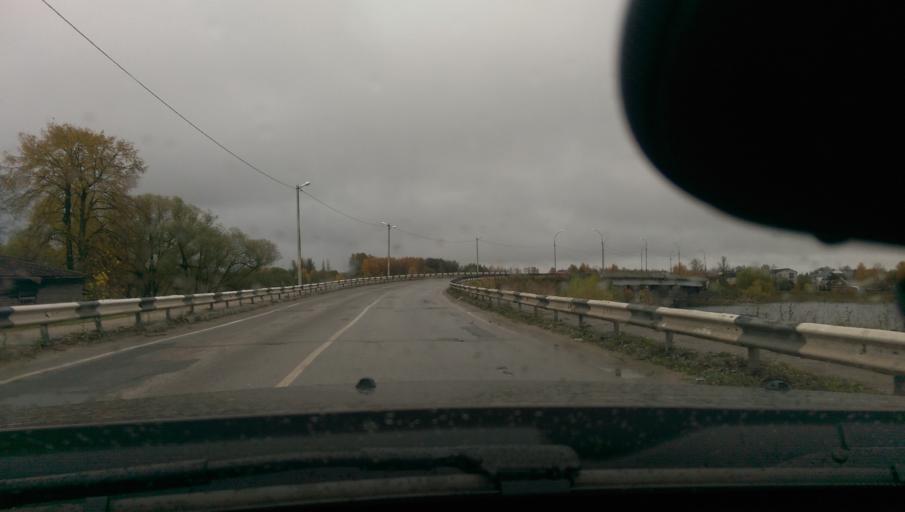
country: RU
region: Jaroslavl
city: Poshekhon'ye
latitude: 58.5078
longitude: 39.1322
